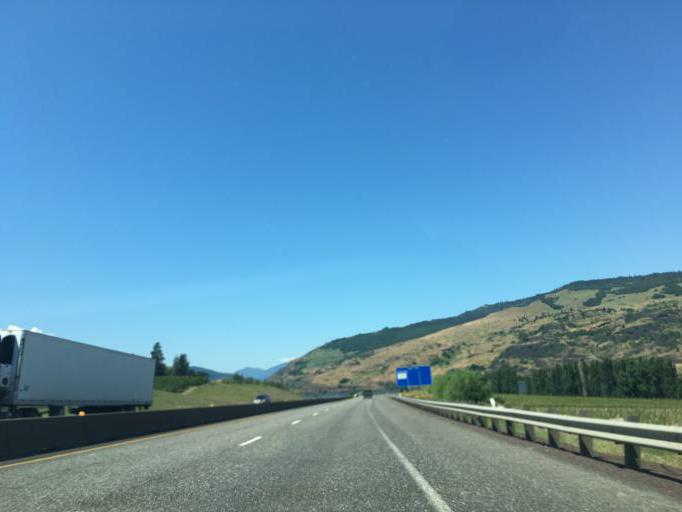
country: US
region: Washington
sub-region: Klickitat County
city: White Salmon
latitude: 45.6947
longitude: -121.3703
